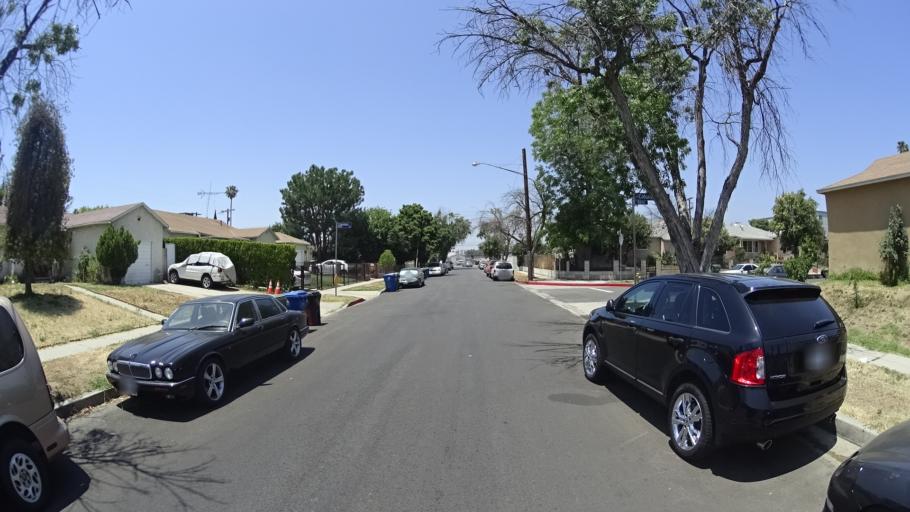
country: US
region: California
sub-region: Los Angeles County
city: Van Nuys
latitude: 34.2201
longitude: -118.4649
